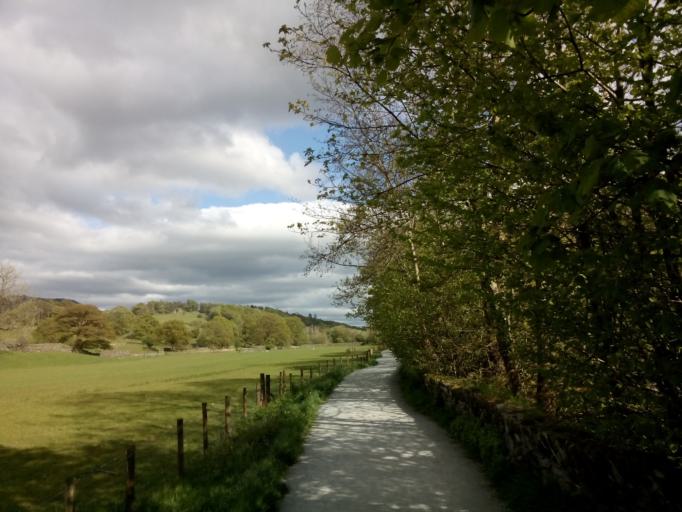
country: GB
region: England
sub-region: Cumbria
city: Ambleside
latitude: 54.4333
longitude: -3.0367
